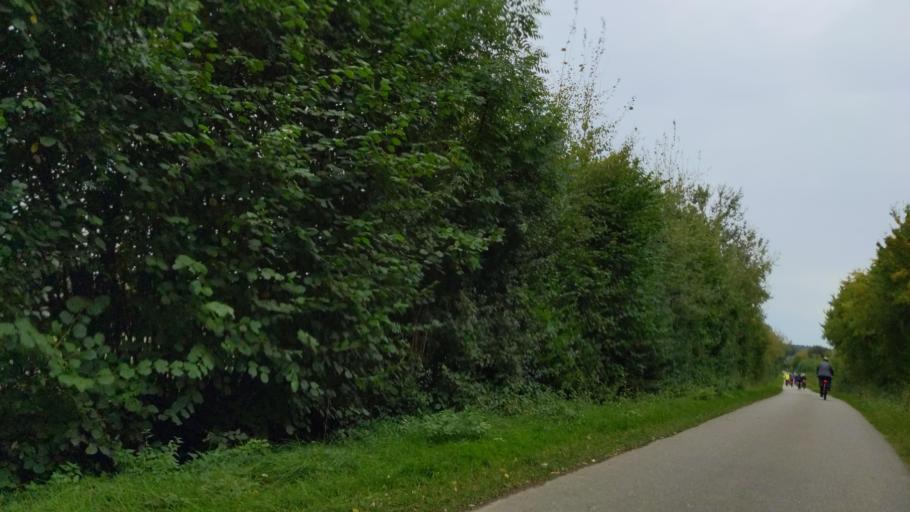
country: DE
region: Schleswig-Holstein
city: Bak
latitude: 53.7204
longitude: 10.7840
